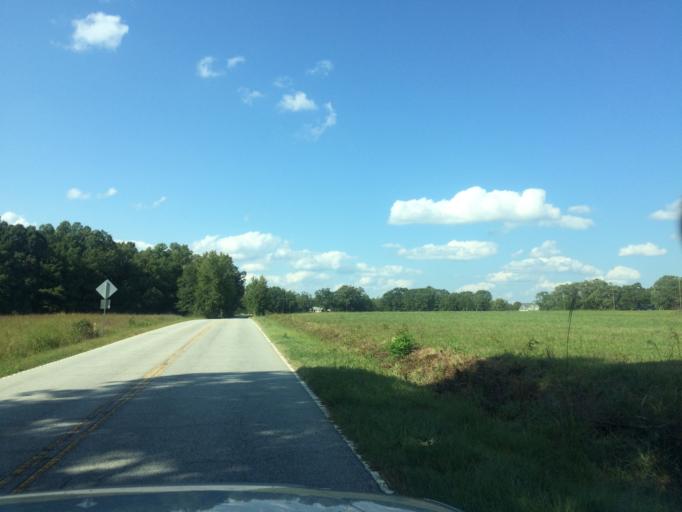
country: US
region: South Carolina
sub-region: Greenwood County
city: Ware Shoals
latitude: 34.4383
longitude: -82.2131
